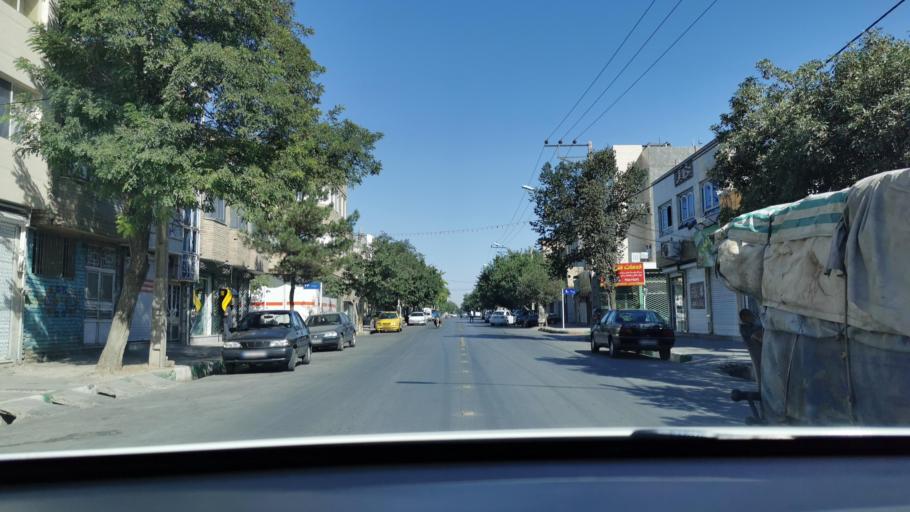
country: IR
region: Razavi Khorasan
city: Mashhad
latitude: 36.3355
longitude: 59.6374
